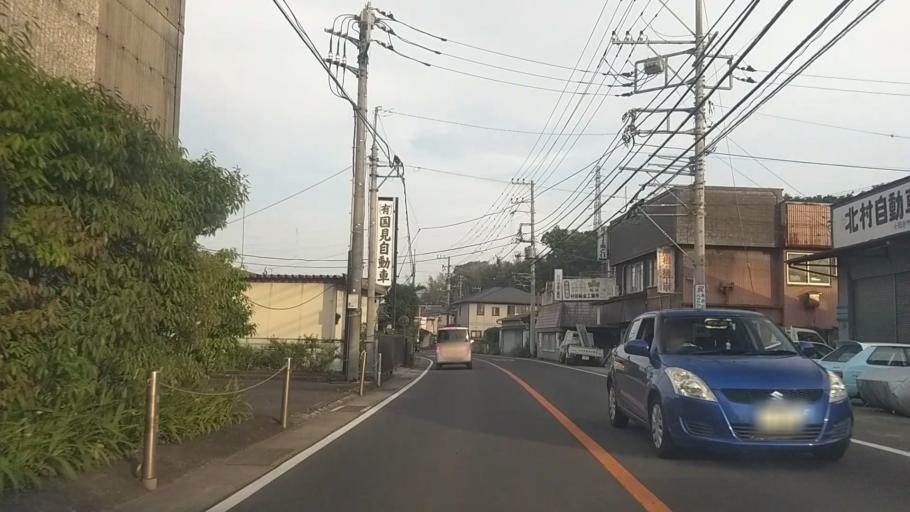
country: JP
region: Kanagawa
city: Odawara
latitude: 35.2844
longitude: 139.1416
